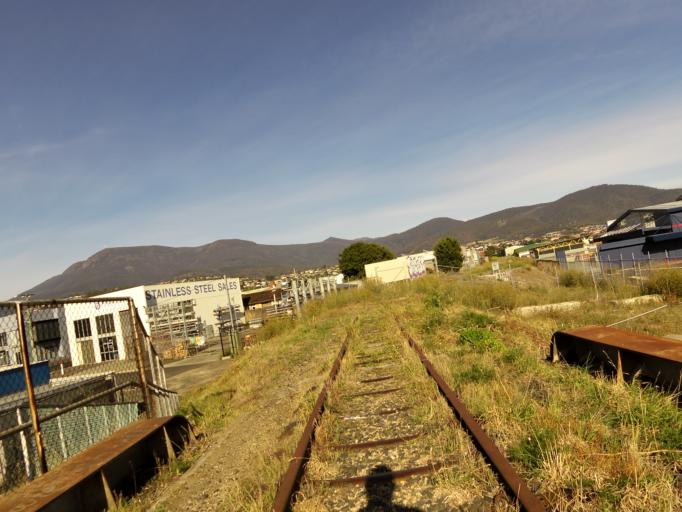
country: AU
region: Tasmania
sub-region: Glenorchy
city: Moonah
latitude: -42.8370
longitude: 147.3021
